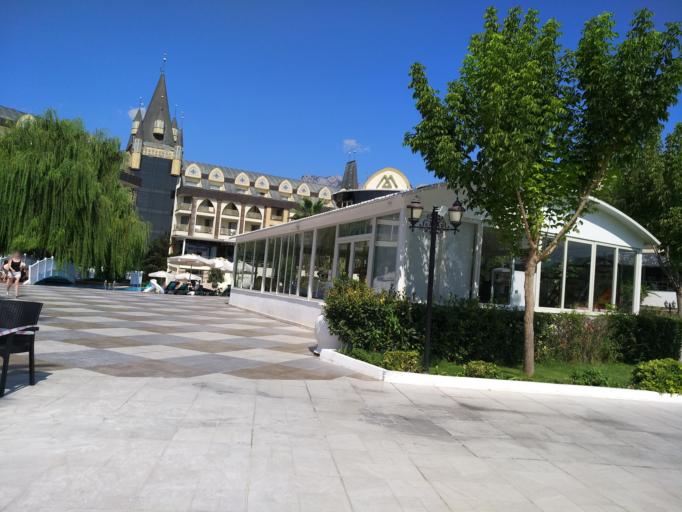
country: TR
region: Antalya
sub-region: Kemer
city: Goeynuek
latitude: 36.6656
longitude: 30.5597
